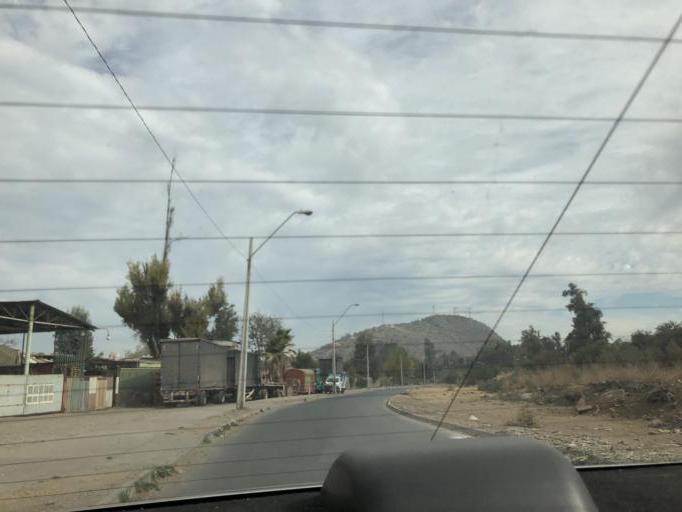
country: CL
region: Santiago Metropolitan
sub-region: Provincia de Cordillera
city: Puente Alto
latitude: -33.6069
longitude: -70.5311
